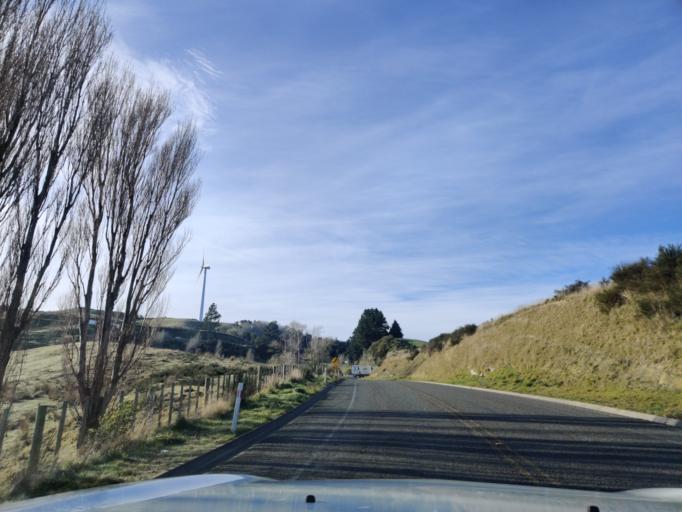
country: NZ
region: Manawatu-Wanganui
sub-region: Palmerston North City
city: Palmerston North
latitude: -40.2866
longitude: 175.7820
